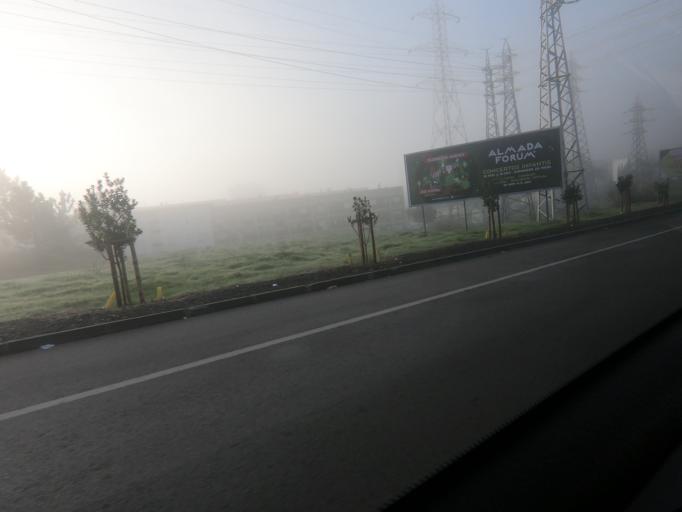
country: PT
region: Setubal
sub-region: Setubal
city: Setubal
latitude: 38.5359
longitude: -8.8608
